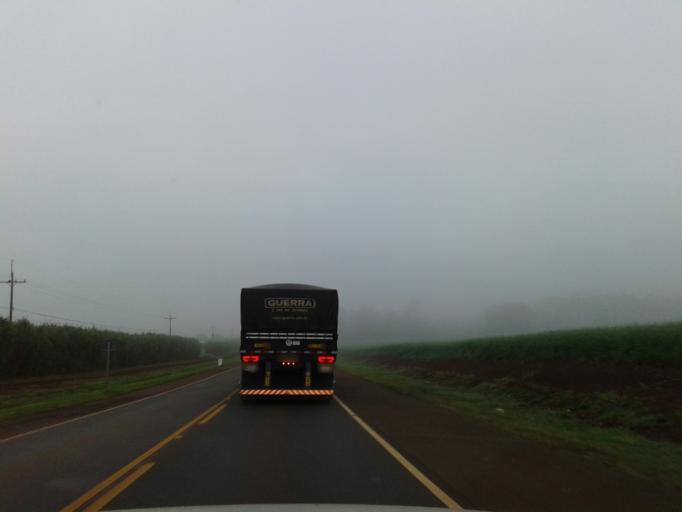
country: PY
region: Itapua
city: Pirapo
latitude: -26.8675
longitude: -55.4572
